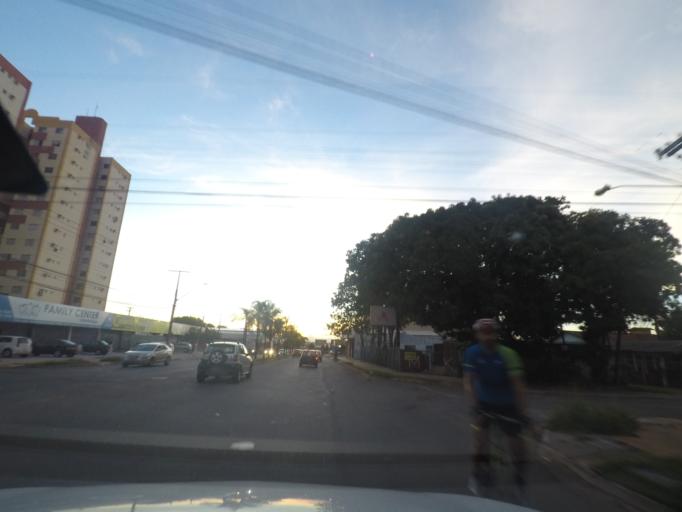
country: BR
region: Goias
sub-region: Goiania
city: Goiania
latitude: -16.6965
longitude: -49.3093
